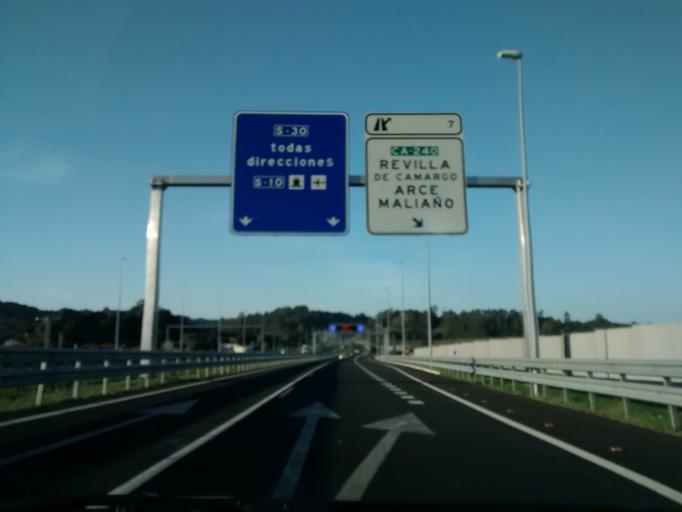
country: ES
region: Cantabria
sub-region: Provincia de Cantabria
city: Camargo
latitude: 43.4000
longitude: -3.8686
